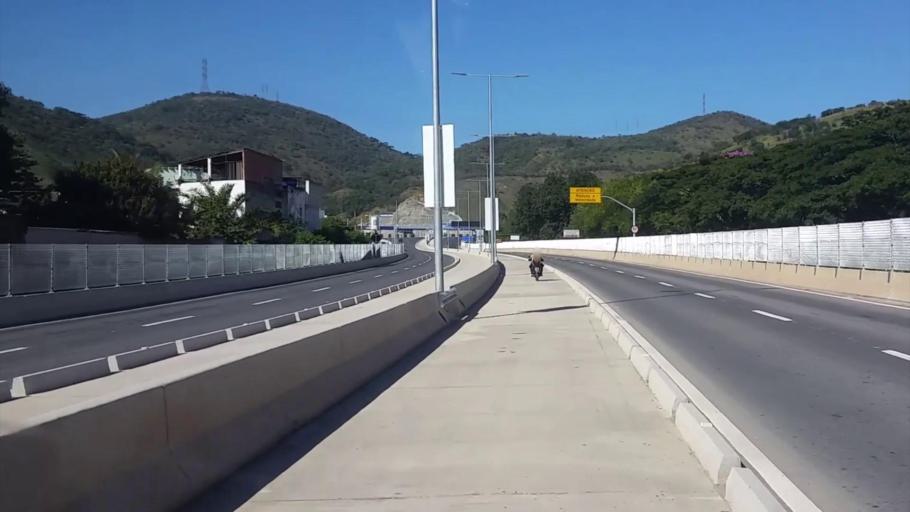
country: BR
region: Rio de Janeiro
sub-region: Nilopolis
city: Nilopolis
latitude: -22.8902
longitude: -43.4008
